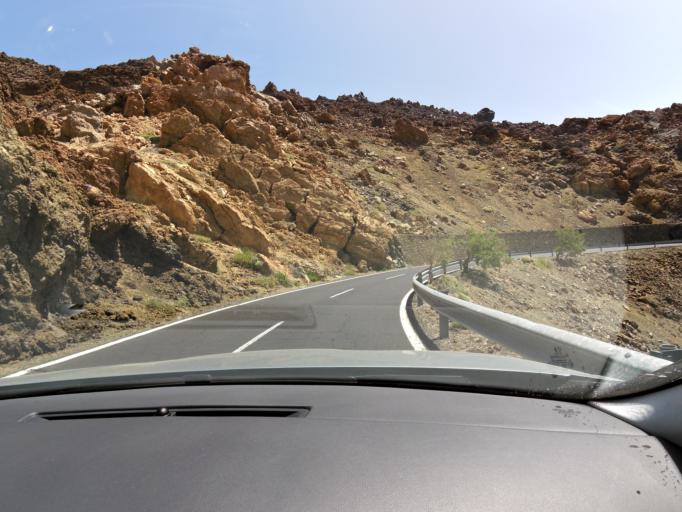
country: ES
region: Canary Islands
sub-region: Provincia de Santa Cruz de Tenerife
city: Los Realejos
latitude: 28.2613
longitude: -16.5967
